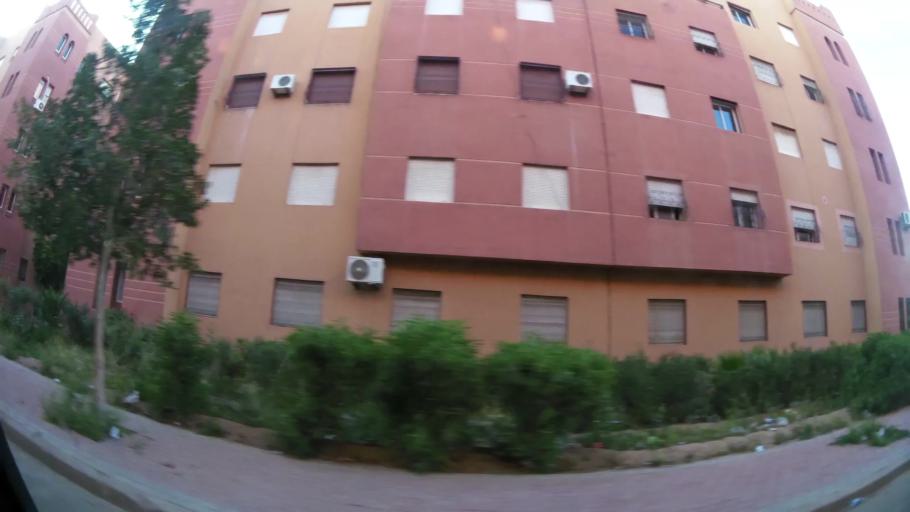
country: MA
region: Marrakech-Tensift-Al Haouz
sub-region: Marrakech
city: Marrakesh
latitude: 31.7520
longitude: -8.1180
